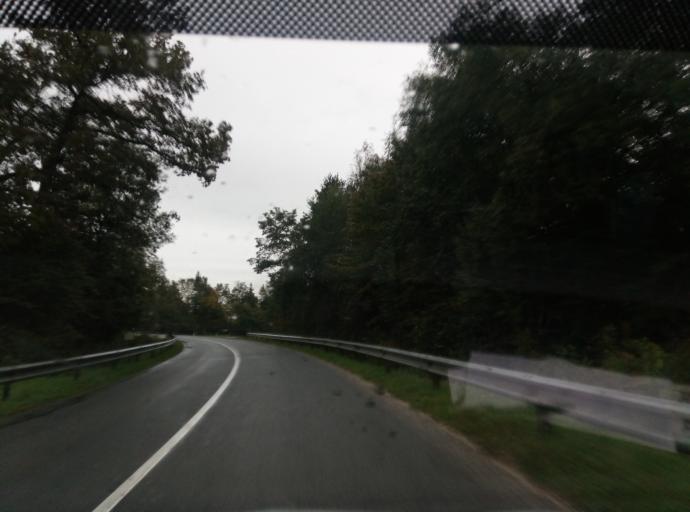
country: SI
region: Medvode
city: Zgornje Pirnice
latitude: 46.1355
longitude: 14.4761
